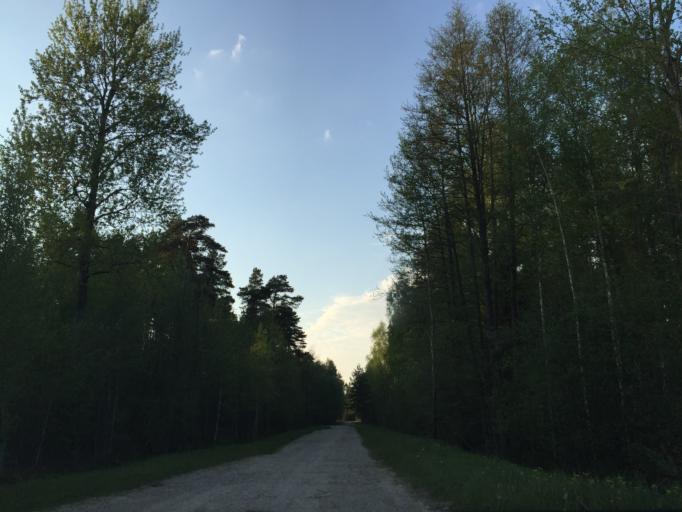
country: LV
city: Tireli
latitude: 56.8885
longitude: 23.6899
